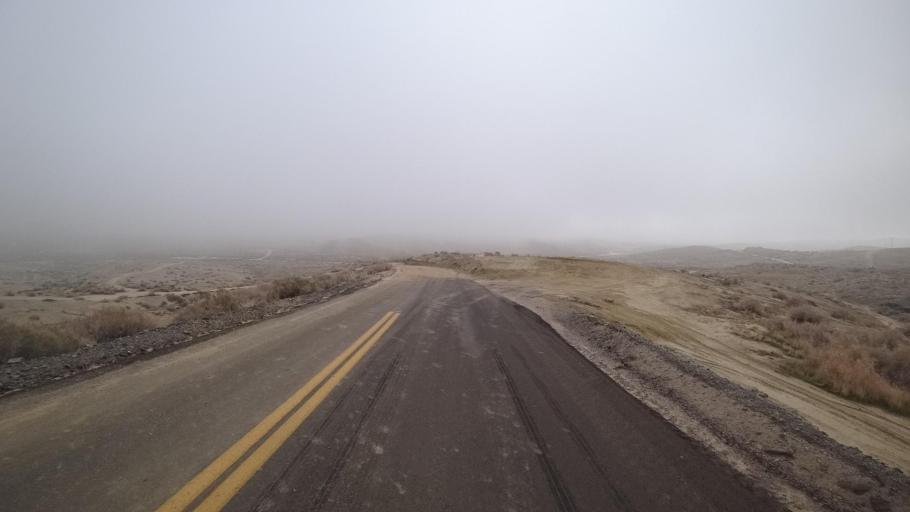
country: US
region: California
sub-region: Kern County
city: Ford City
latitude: 35.1599
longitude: -119.3763
